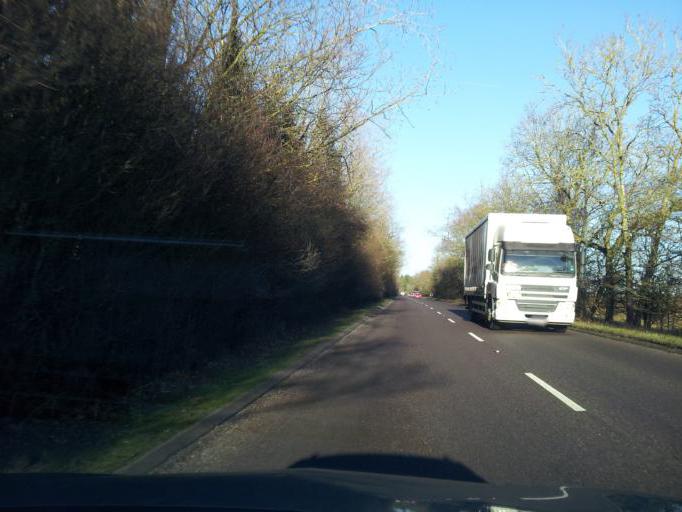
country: GB
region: England
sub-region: Suffolk
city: Lavenham
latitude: 52.1306
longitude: 0.7523
